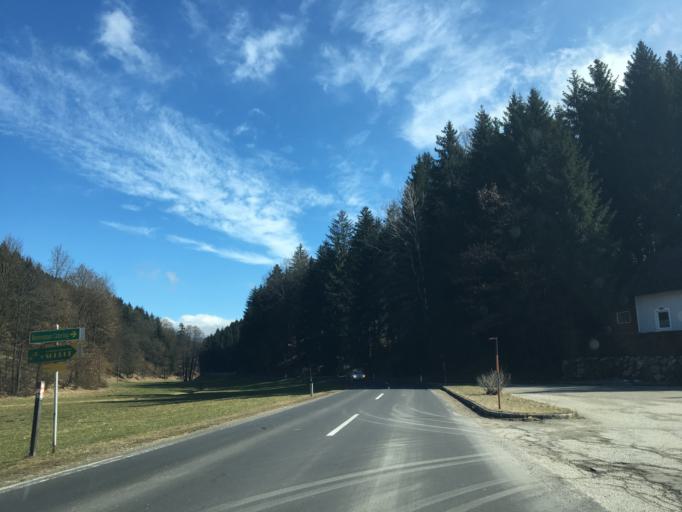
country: AT
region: Lower Austria
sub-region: Politischer Bezirk Melk
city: Dorfstetten
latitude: 48.2761
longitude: 14.9227
